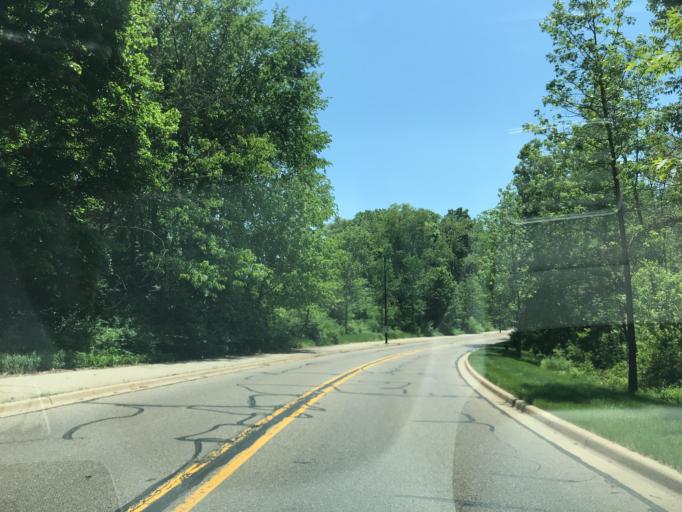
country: US
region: Michigan
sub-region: Washtenaw County
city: Ann Arbor
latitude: 42.2867
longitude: -83.7114
